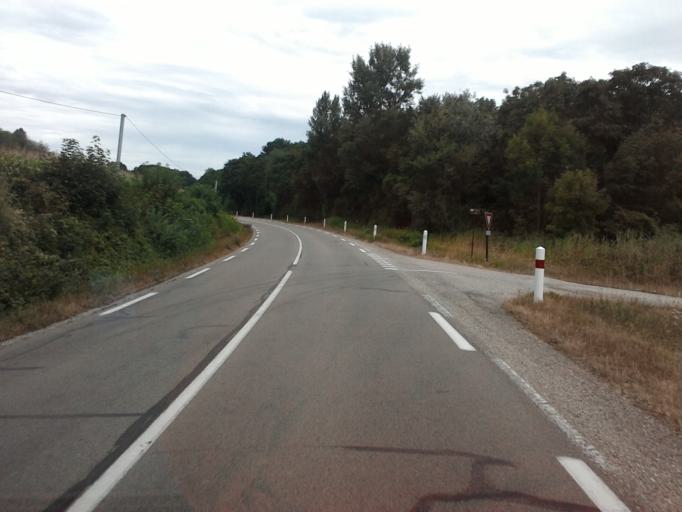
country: FR
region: Rhone-Alpes
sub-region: Departement de l'Isere
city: Faverges-de-la-Tour
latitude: 45.5946
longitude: 5.5377
